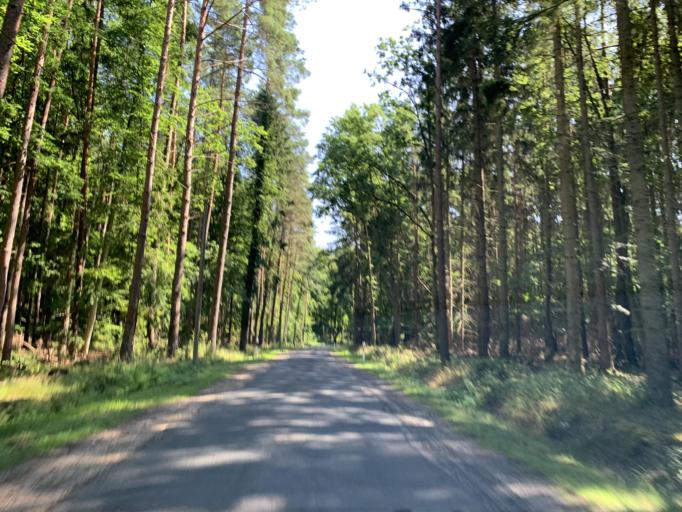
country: DE
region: Mecklenburg-Vorpommern
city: Carpin
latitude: 53.3179
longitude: 13.2489
